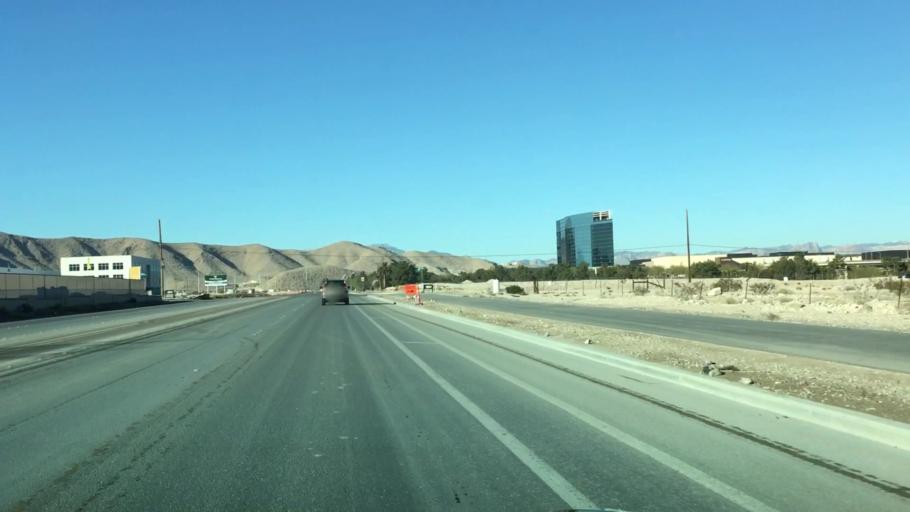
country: US
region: Nevada
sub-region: Clark County
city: Enterprise
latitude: 35.9629
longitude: -115.1622
